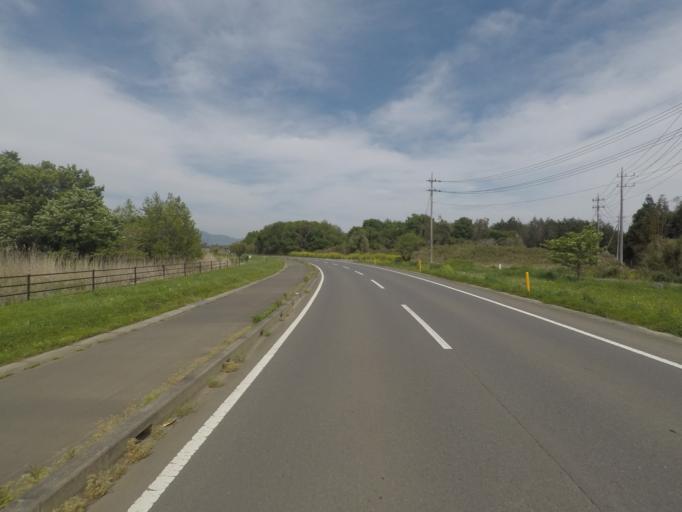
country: JP
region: Ibaraki
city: Ishige
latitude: 36.1534
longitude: 140.0315
